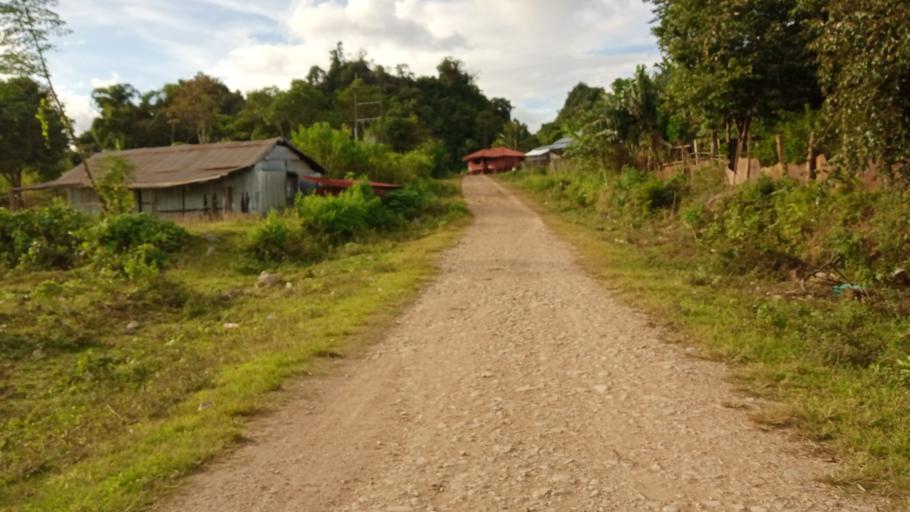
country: LA
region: Xiangkhoang
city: Phonsavan
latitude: 19.1095
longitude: 102.9257
